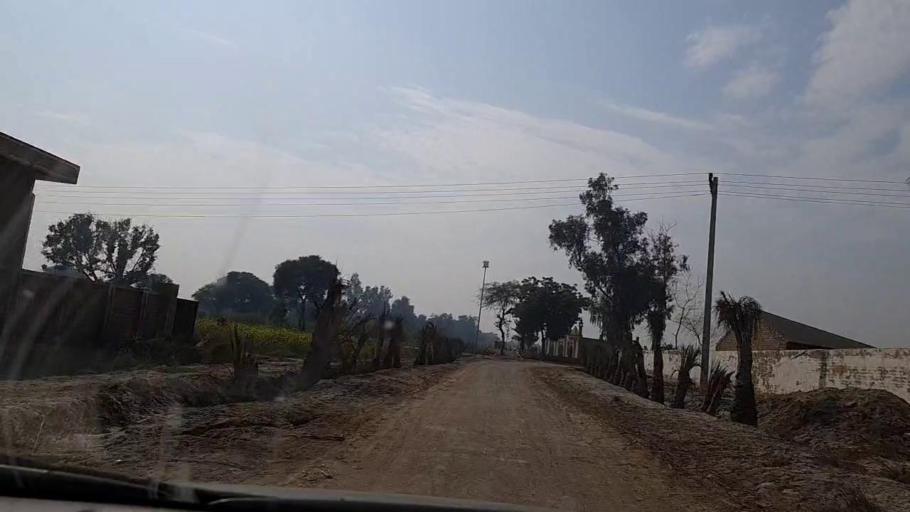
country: PK
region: Sindh
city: Daulatpur
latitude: 26.5329
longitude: 67.9857
